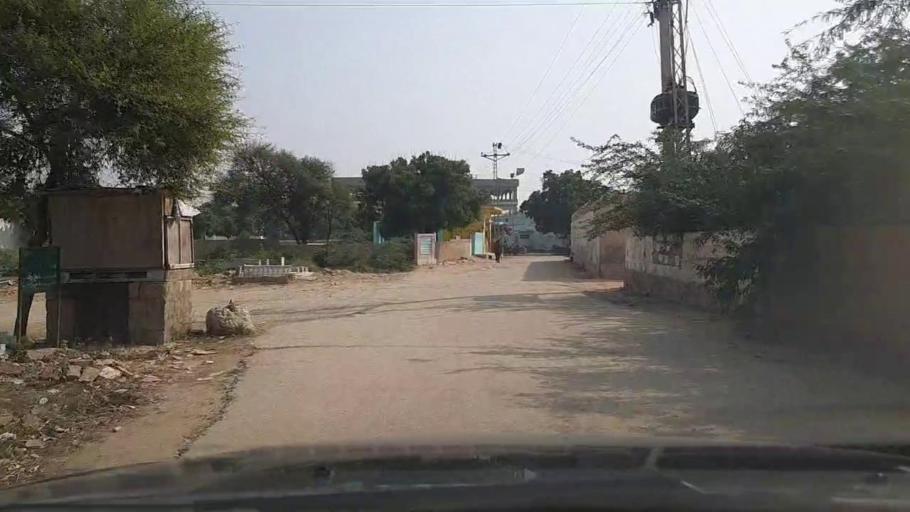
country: PK
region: Sindh
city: Thatta
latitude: 24.7459
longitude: 67.8983
